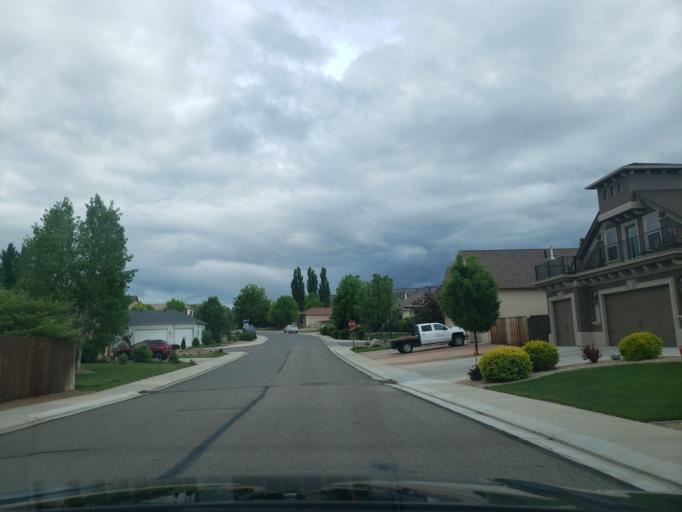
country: US
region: Colorado
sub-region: Mesa County
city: Redlands
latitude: 39.1065
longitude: -108.6684
